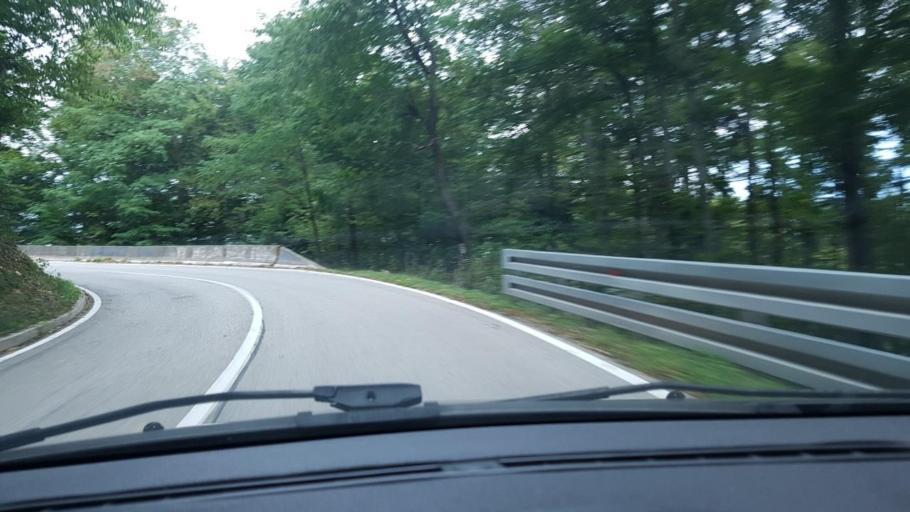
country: HR
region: Grad Zagreb
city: Kasina
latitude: 45.9388
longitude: 15.9757
